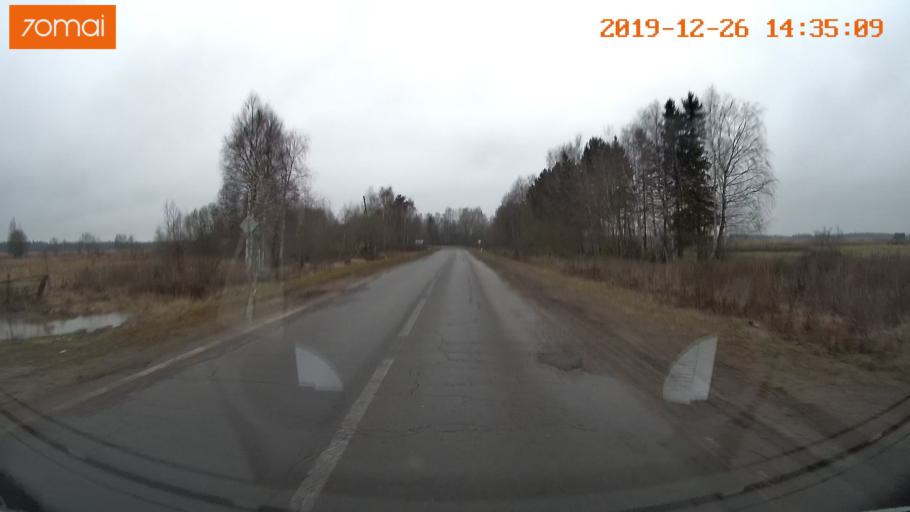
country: RU
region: Jaroslavl
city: Poshekhon'ye
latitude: 58.4226
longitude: 38.9893
